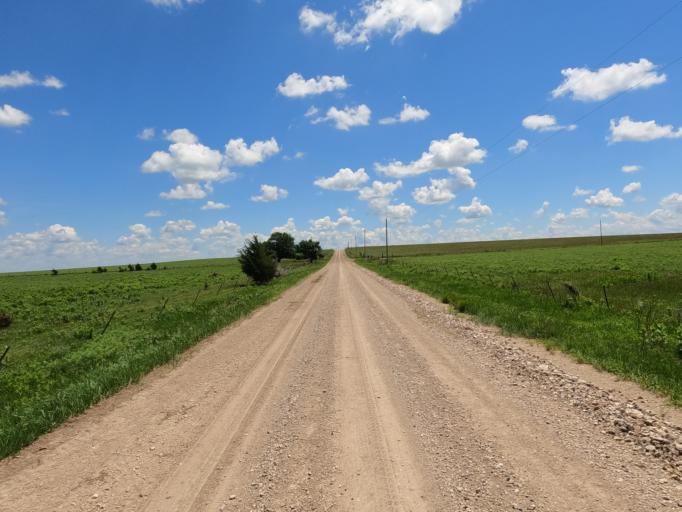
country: US
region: Kansas
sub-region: Chase County
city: Cottonwood Falls
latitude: 38.2168
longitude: -96.7509
